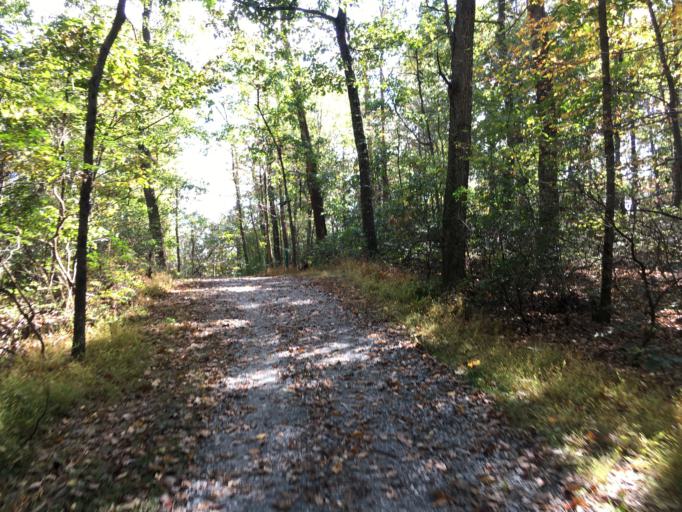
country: US
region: Pennsylvania
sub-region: York County
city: Yorklyn
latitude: 40.0117
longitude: -76.6423
